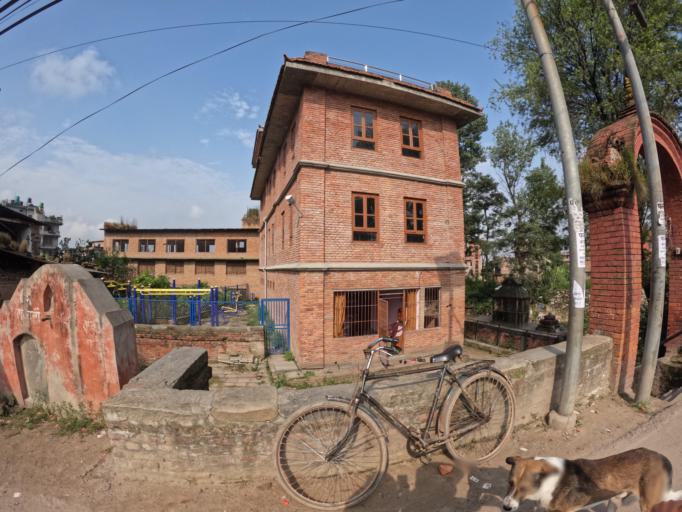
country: NP
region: Central Region
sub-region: Bagmati Zone
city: Bhaktapur
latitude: 27.6793
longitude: 85.4295
